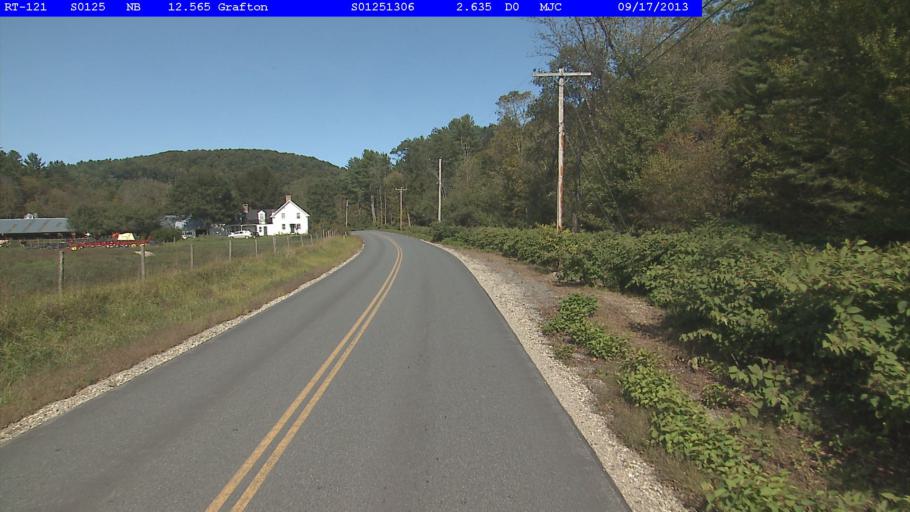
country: US
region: Vermont
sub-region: Windsor County
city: Chester
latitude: 43.1761
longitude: -72.5822
